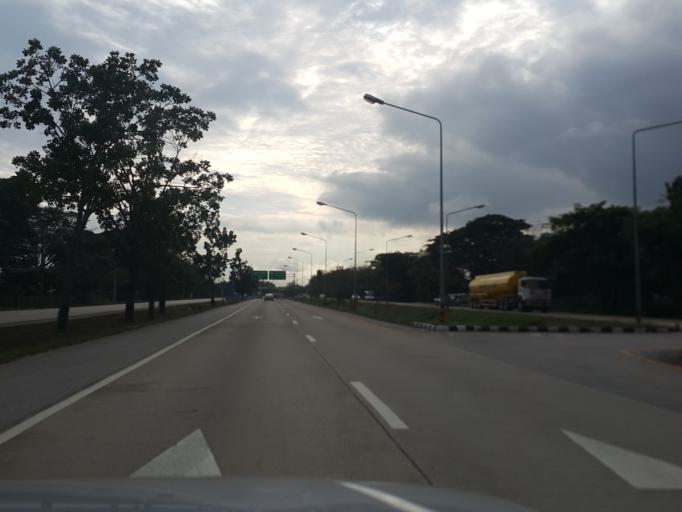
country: TH
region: Lampang
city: Lampang
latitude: 18.2434
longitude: 99.4459
